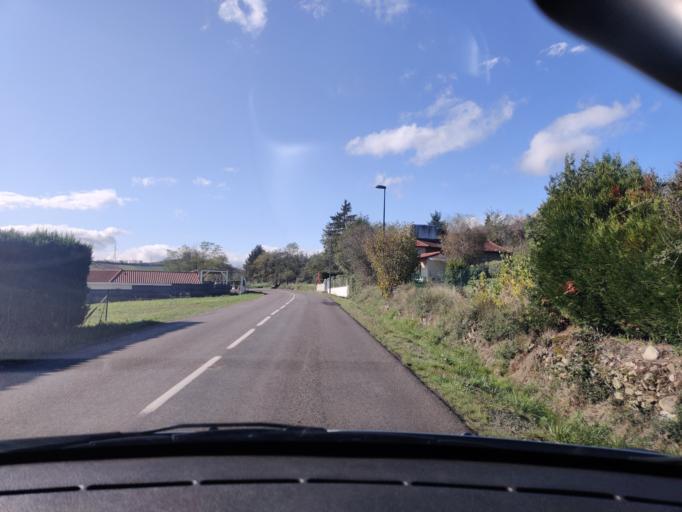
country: FR
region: Auvergne
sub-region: Departement du Puy-de-Dome
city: Combronde
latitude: 45.9913
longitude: 3.1239
